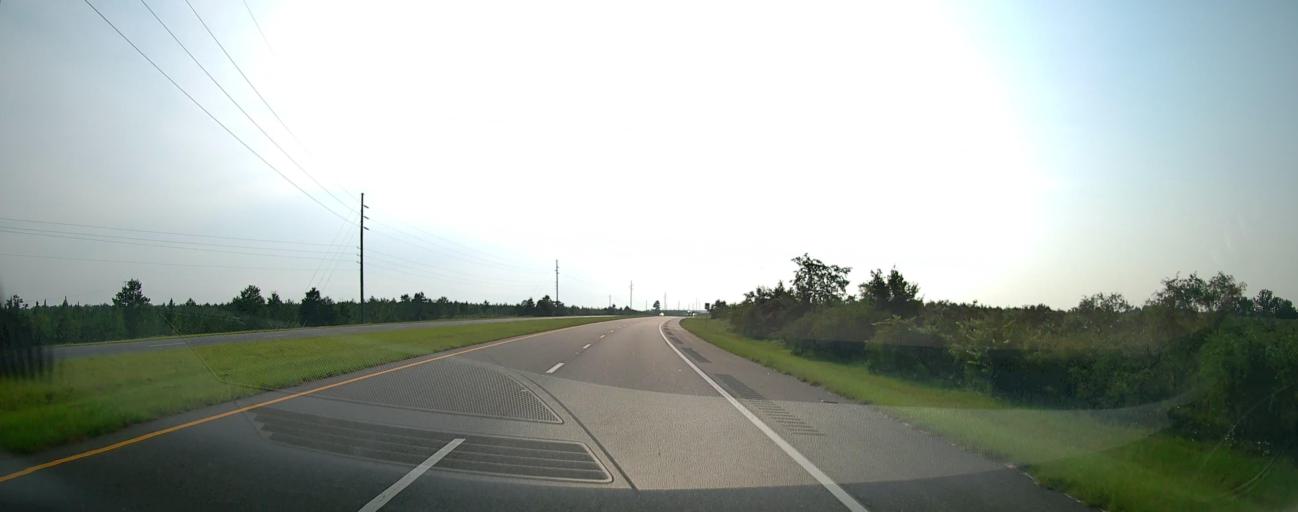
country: US
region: Georgia
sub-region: Talbot County
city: Talbotton
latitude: 32.5949
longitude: -84.4375
